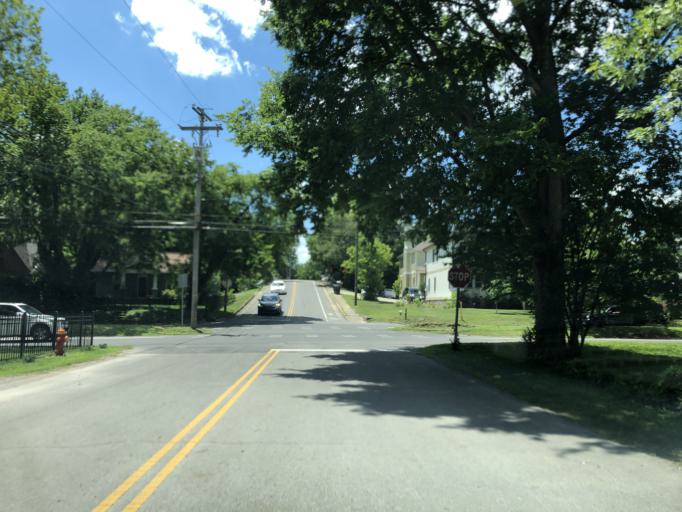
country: US
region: Tennessee
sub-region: Davidson County
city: Nashville
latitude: 36.1881
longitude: -86.7262
